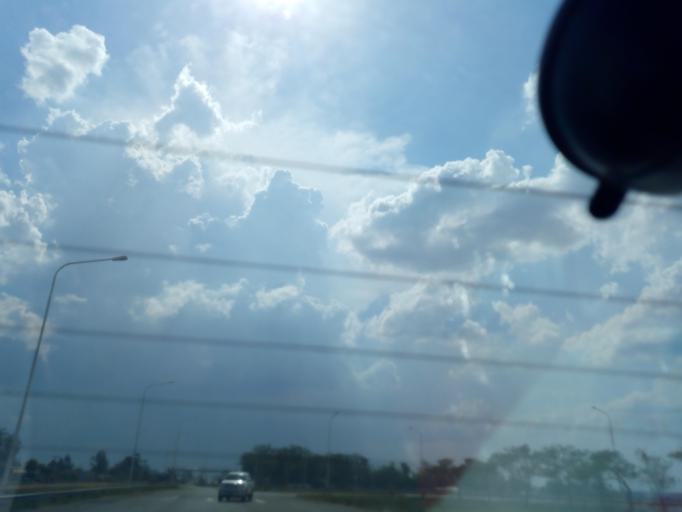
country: AR
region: Corrientes
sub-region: Departamento de Paso de los Libres
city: Paso de los Libres
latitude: -29.7219
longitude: -57.1489
